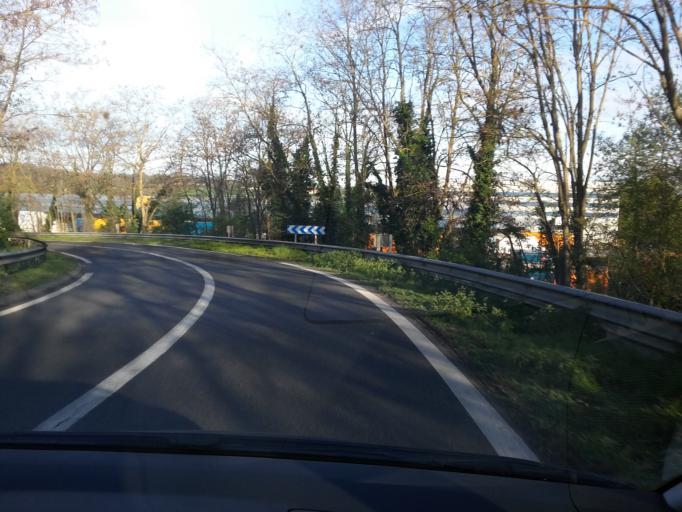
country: FR
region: Picardie
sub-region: Departement de l'Oise
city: Le Meux
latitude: 49.3581
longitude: 2.7595
